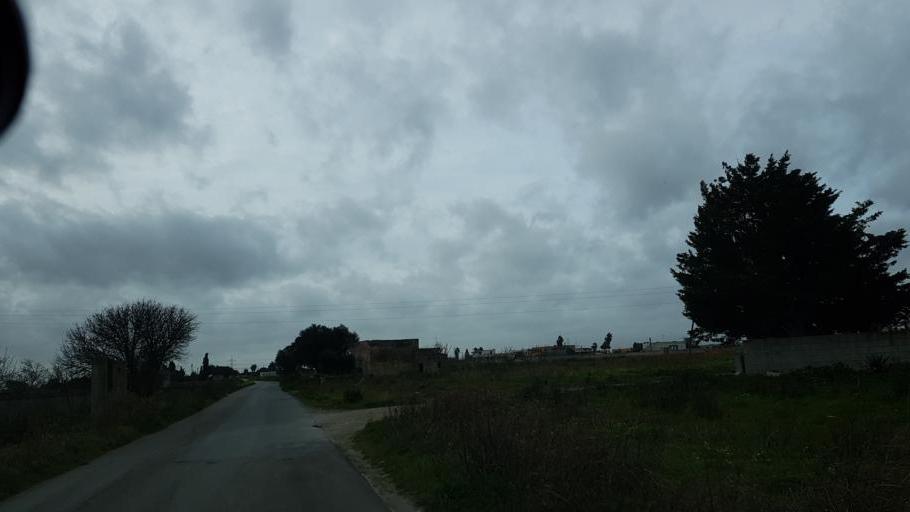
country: IT
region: Apulia
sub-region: Provincia di Brindisi
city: Brindisi
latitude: 40.6115
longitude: 17.9268
